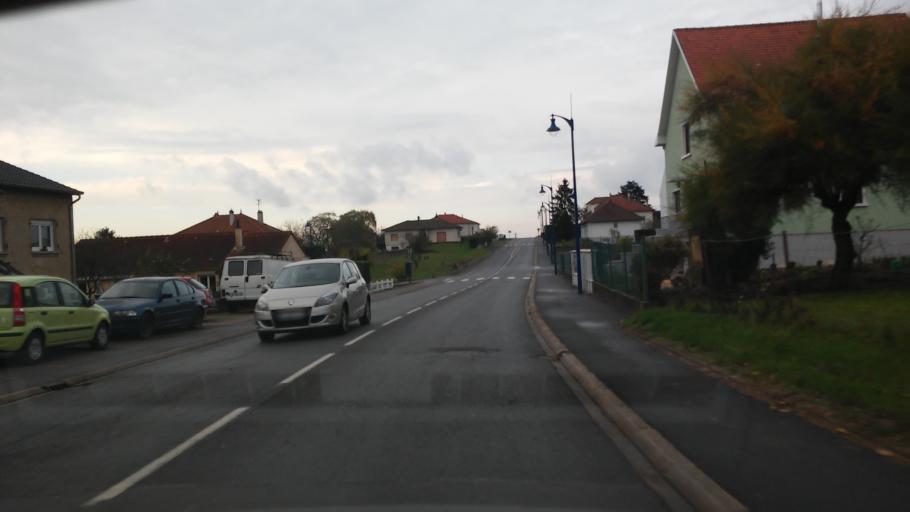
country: FR
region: Lorraine
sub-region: Departement de la Moselle
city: Ennery
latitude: 49.2094
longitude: 6.2346
